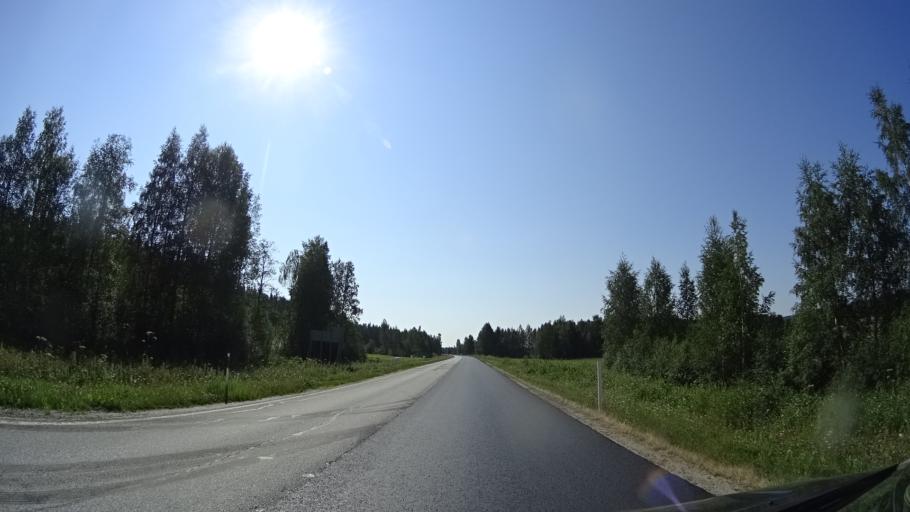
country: FI
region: North Karelia
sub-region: Joensuu
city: Juuka
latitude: 63.2146
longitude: 29.3048
